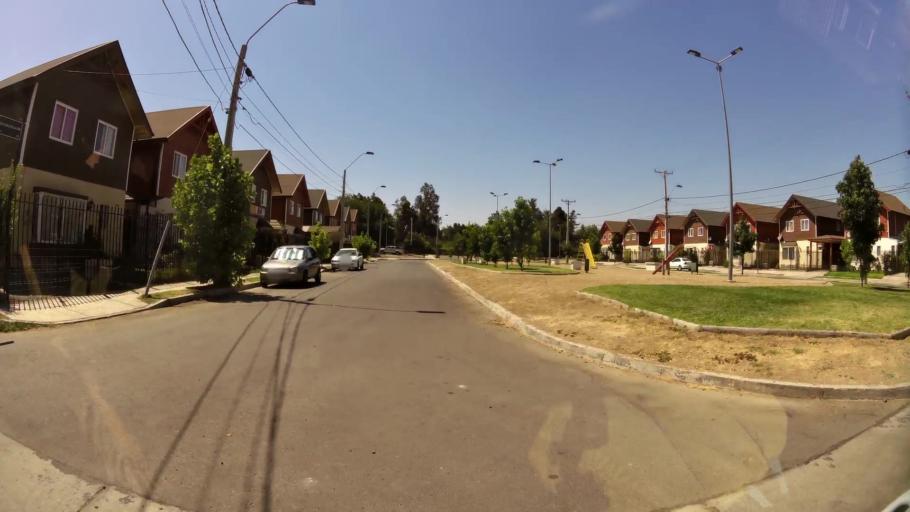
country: CL
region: Maule
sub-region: Provincia de Curico
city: Curico
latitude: -34.9648
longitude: -71.2307
